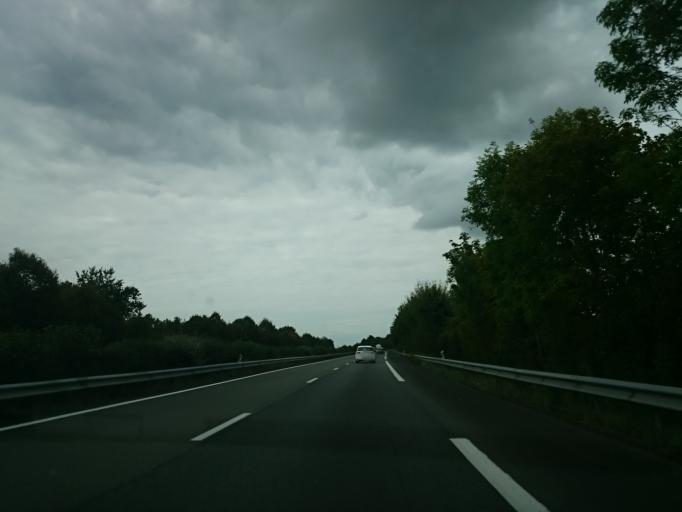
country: FR
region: Pays de la Loire
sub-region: Departement de la Loire-Atlantique
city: Heric
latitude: 47.4713
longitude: -1.6375
